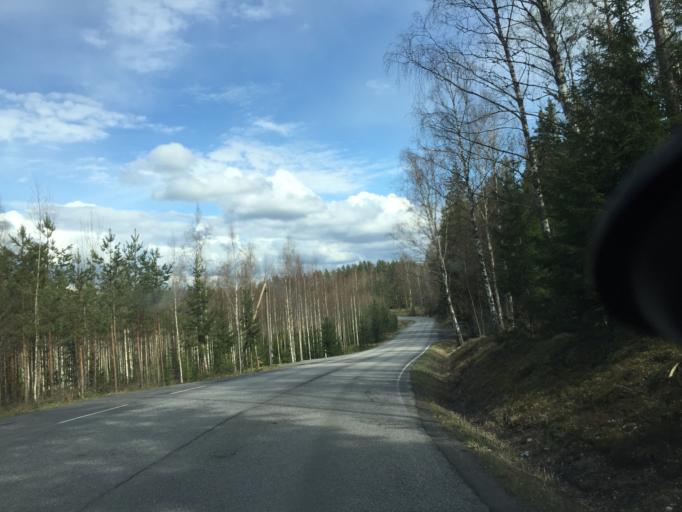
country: FI
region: Varsinais-Suomi
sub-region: Salo
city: Pernioe
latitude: 60.0442
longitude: 23.2500
